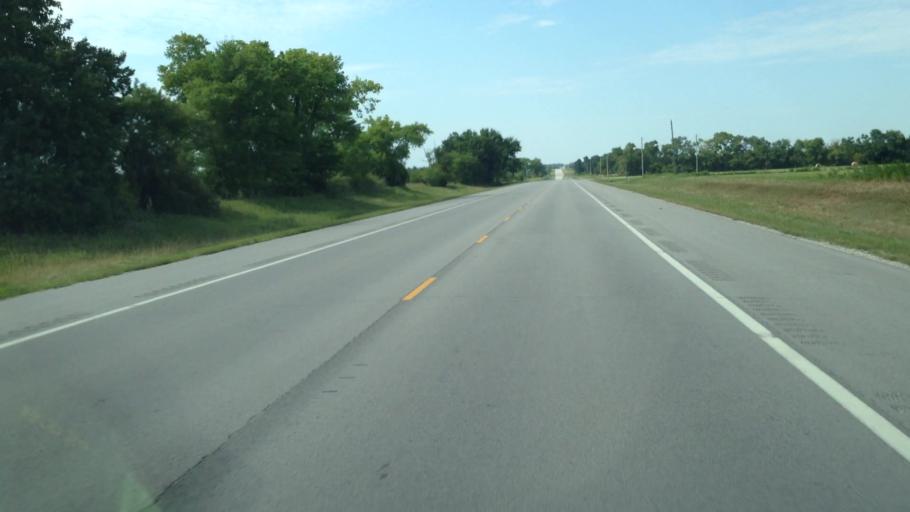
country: US
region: Kansas
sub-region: Labette County
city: Altamont
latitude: 37.2590
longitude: -95.2672
